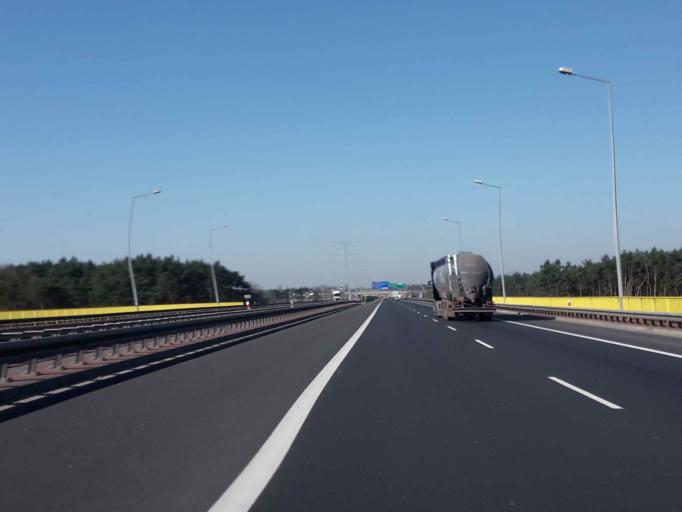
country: PL
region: Greater Poland Voivodeship
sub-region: Powiat poznanski
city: Lubon
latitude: 52.3528
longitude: 16.9170
